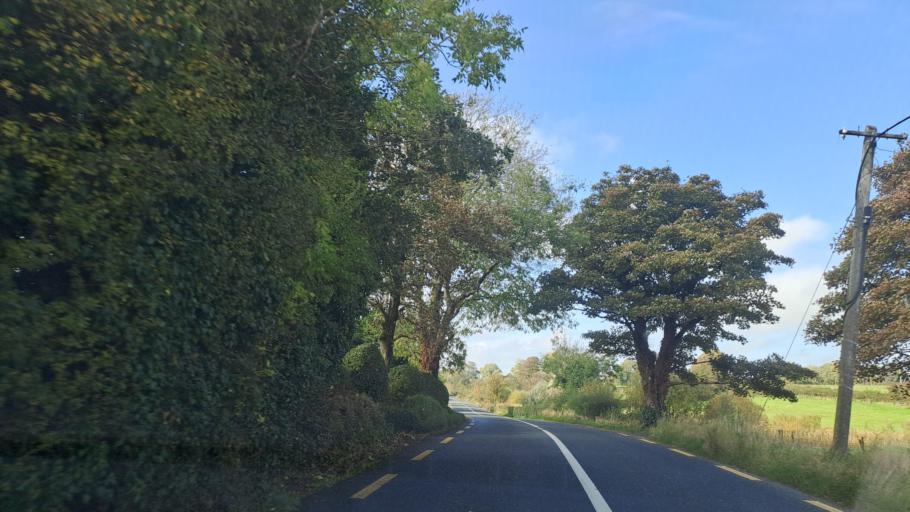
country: IE
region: Ulster
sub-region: An Cabhan
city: Cootehill
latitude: 54.0573
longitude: -7.0205
